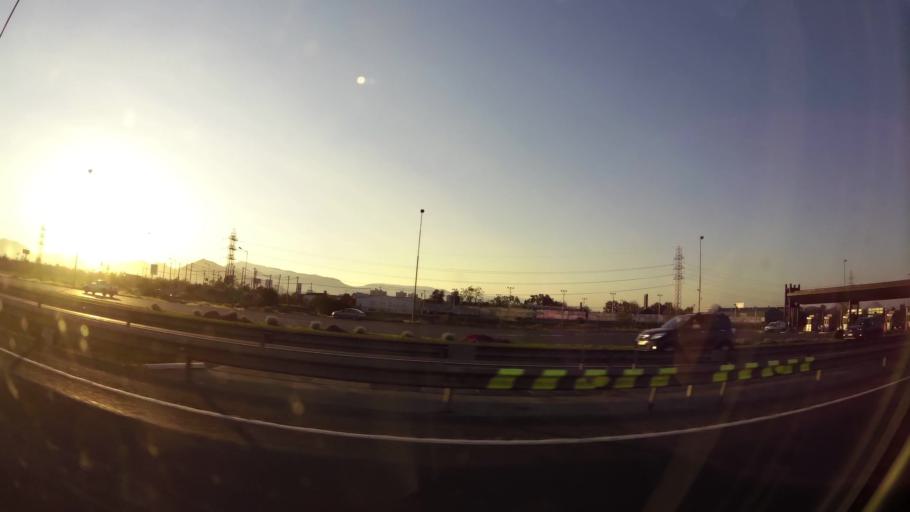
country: CL
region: Santiago Metropolitan
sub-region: Provincia de Santiago
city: Lo Prado
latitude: -33.4884
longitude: -70.7466
